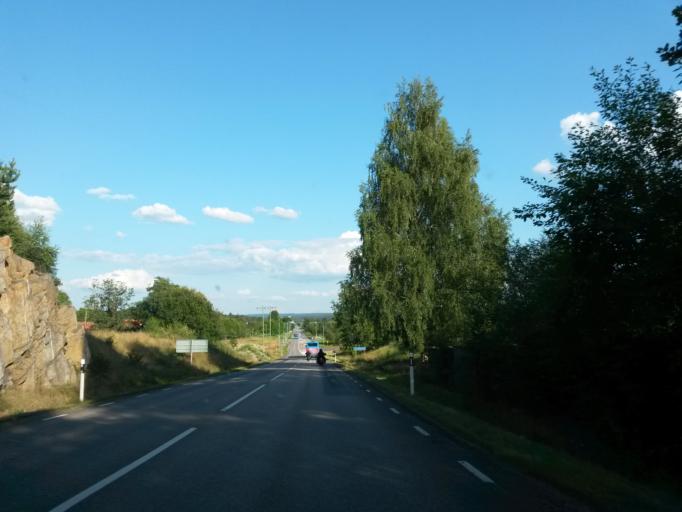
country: SE
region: Vaestra Goetaland
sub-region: Alingsas Kommun
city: Alingsas
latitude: 57.9486
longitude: 12.5015
